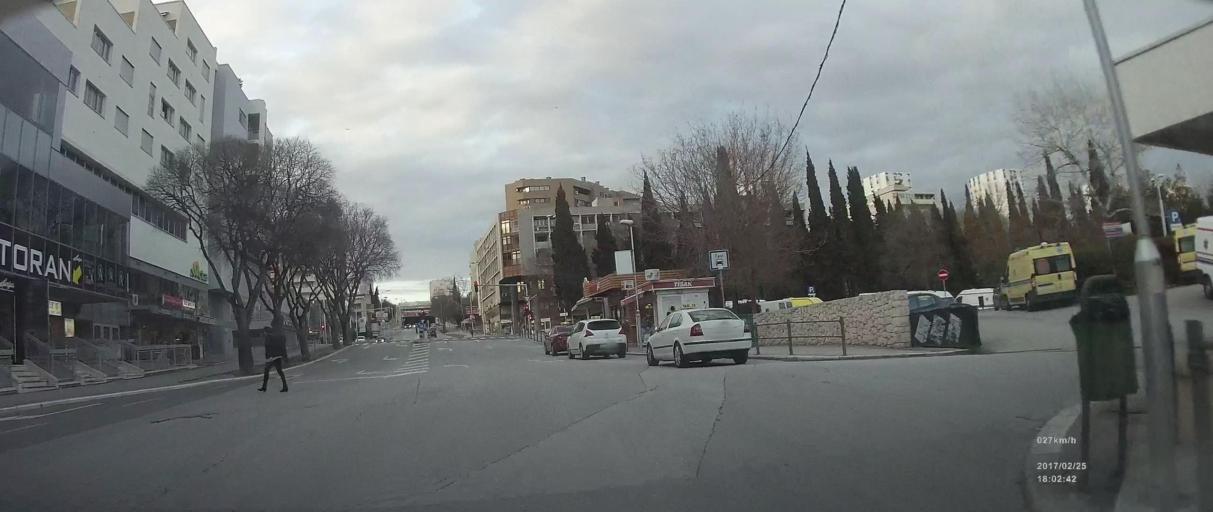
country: HR
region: Splitsko-Dalmatinska
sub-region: Grad Split
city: Split
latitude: 43.5043
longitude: 16.4565
